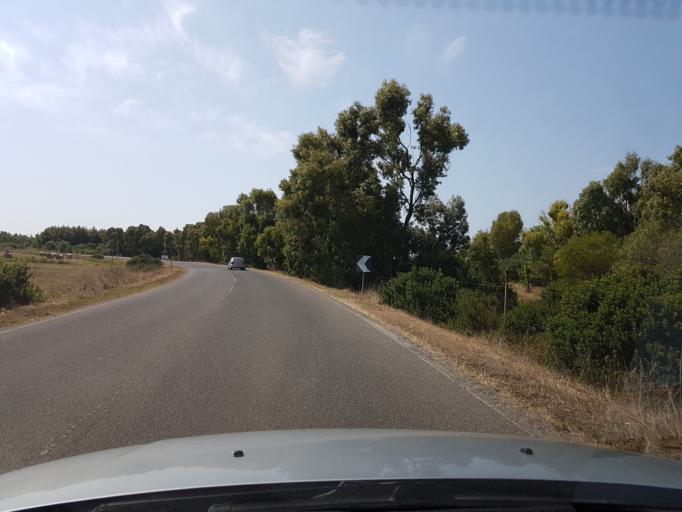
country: IT
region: Sardinia
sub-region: Provincia di Oristano
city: Cabras
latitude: 39.9184
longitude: 8.4963
